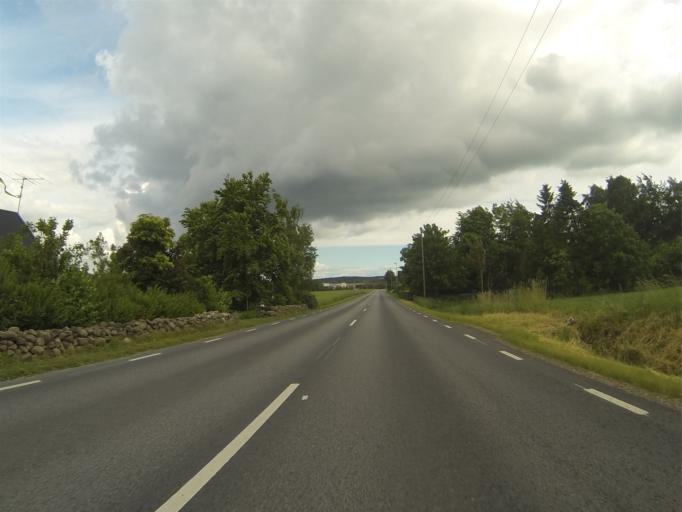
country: SE
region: Skane
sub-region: Eslovs Kommun
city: Eslov
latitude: 55.7304
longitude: 13.3361
